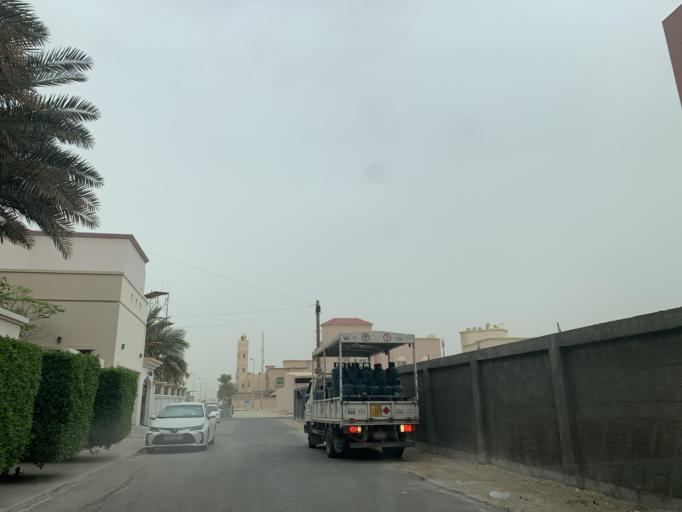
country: BH
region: Northern
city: Ar Rifa'
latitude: 26.1470
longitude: 50.5292
